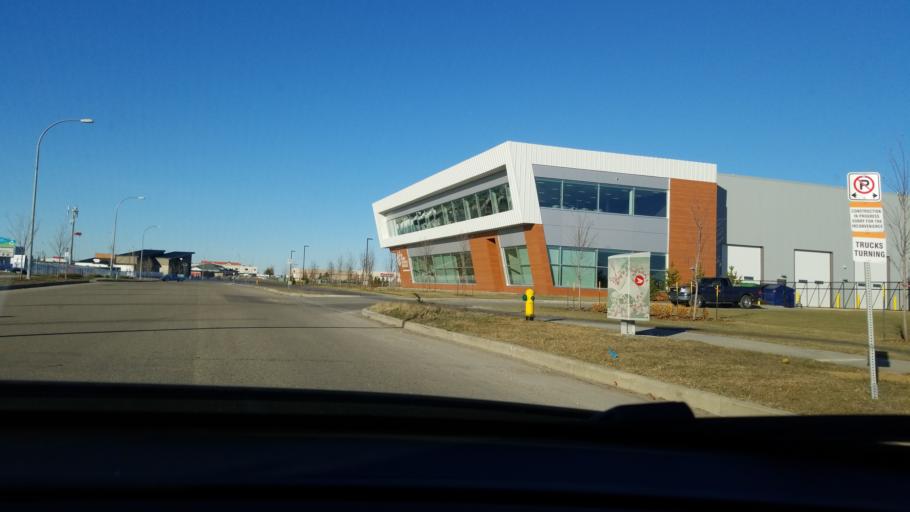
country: CA
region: Alberta
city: Sherwood Park
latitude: 53.5453
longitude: -113.3082
